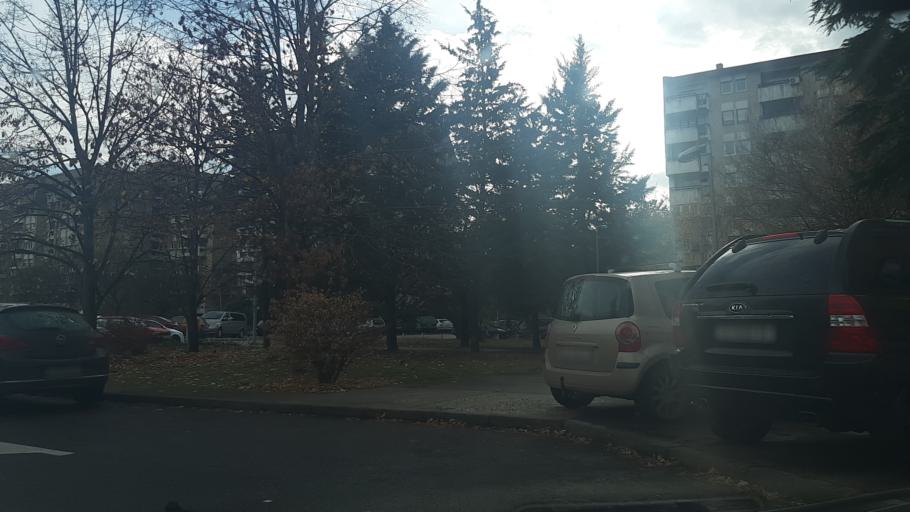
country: MK
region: Karpos
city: Skopje
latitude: 41.9909
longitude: 21.4493
